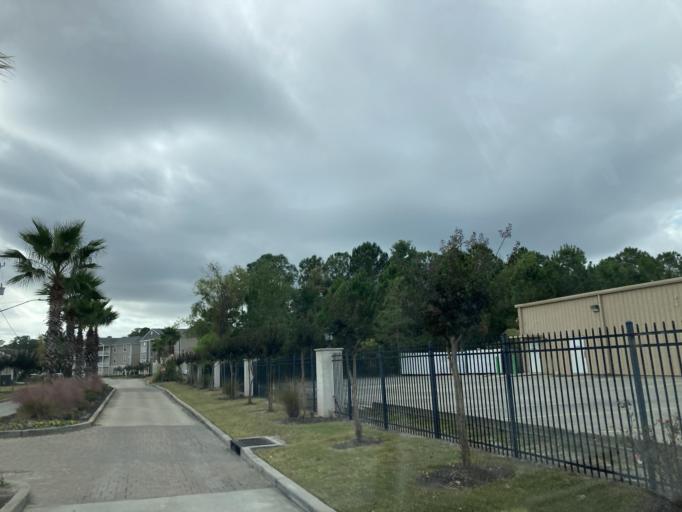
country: US
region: Mississippi
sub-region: Jackson County
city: Gulf Hills
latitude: 30.4387
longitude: -88.8345
